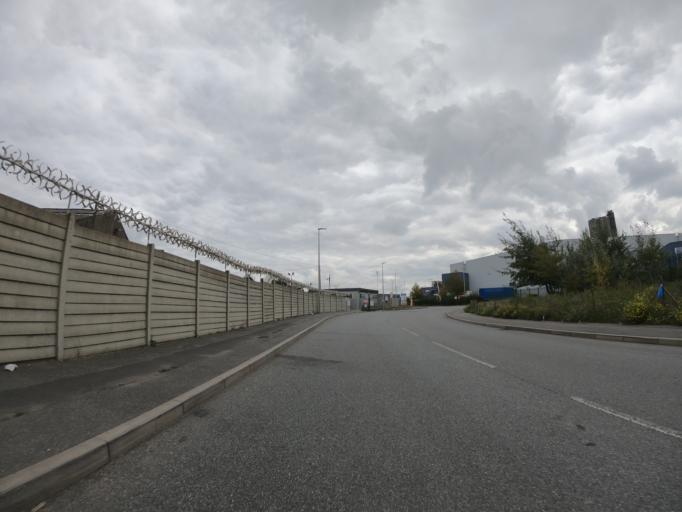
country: GB
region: England
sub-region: Greater London
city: Erith
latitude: 51.4960
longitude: 0.1683
